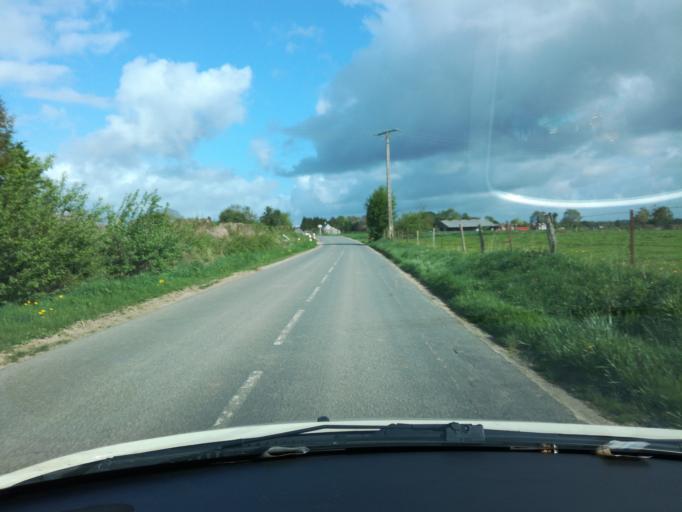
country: FR
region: Picardie
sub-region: Departement de la Somme
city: Hornoy-le-Bourg
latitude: 49.8632
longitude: 1.8424
